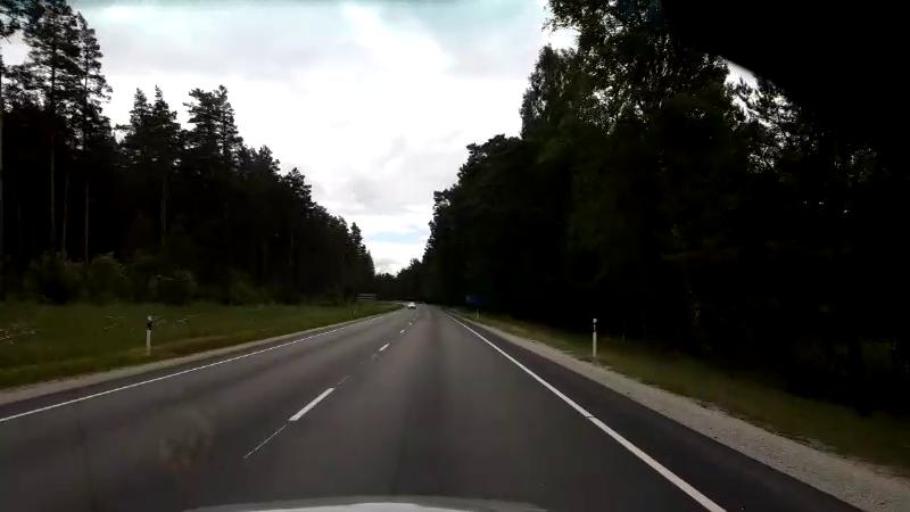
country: EE
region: Paernumaa
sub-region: Paernu linn
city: Parnu
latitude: 58.1490
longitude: 24.5005
